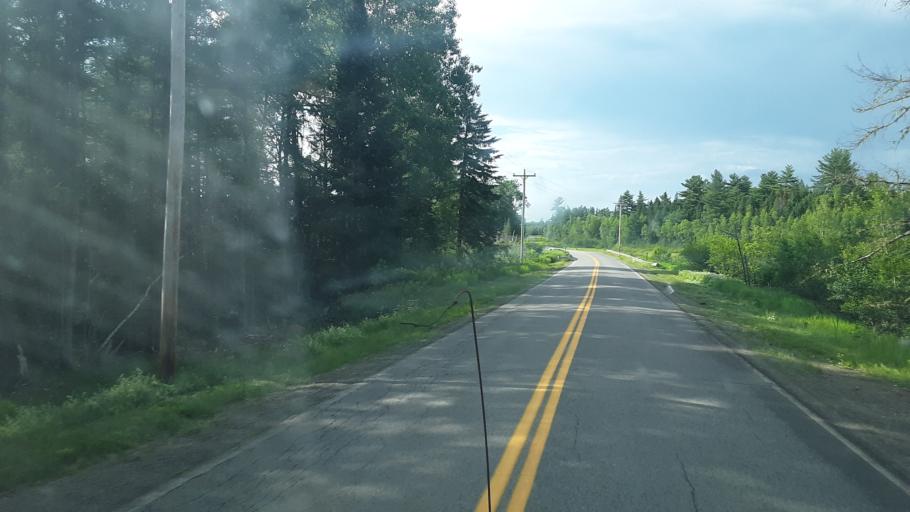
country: US
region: Maine
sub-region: Washington County
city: Calais
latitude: 45.1774
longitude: -67.5151
